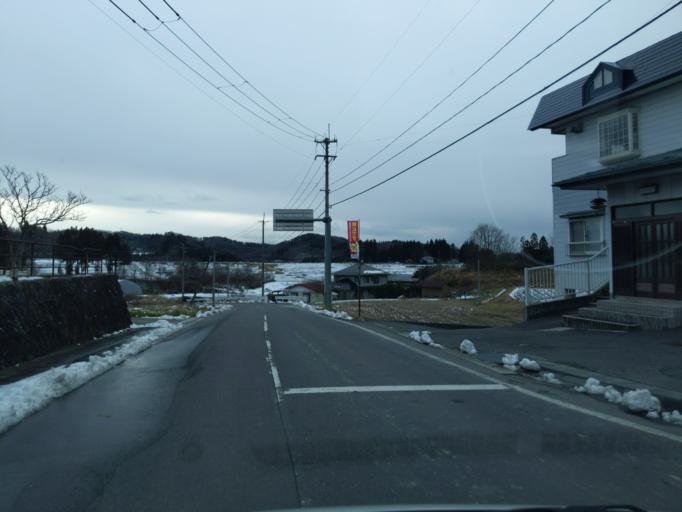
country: JP
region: Iwate
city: Mizusawa
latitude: 39.1833
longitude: 141.2454
